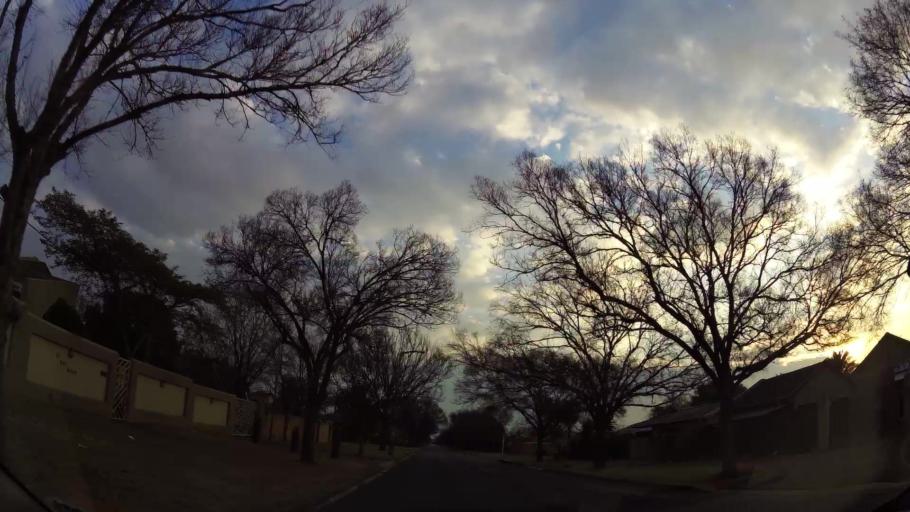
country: ZA
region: Gauteng
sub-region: Ekurhuleni Metropolitan Municipality
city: Benoni
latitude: -26.1636
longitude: 28.3033
